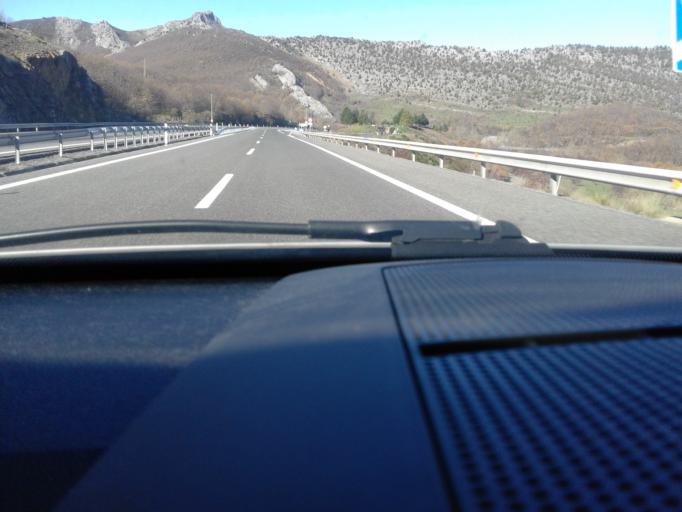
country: ES
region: Castille and Leon
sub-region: Provincia de Leon
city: Soto y Amio
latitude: 42.8660
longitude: -5.8799
